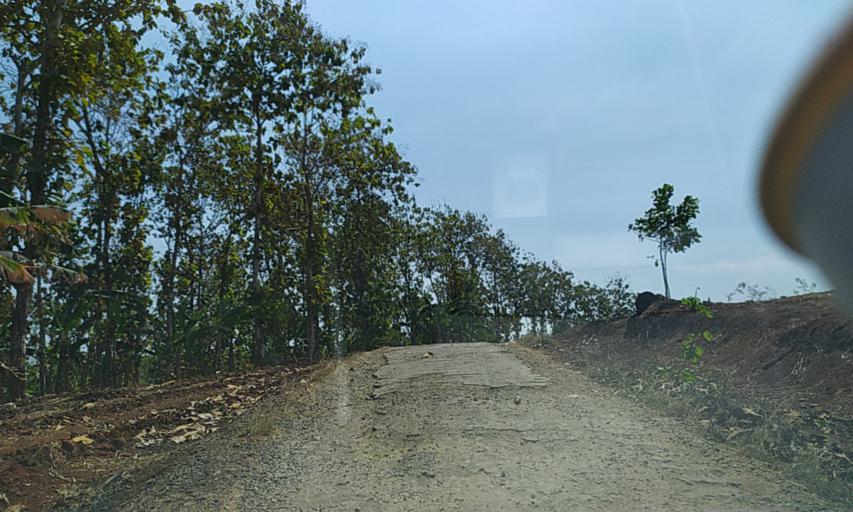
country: ID
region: Central Java
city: Prapagan
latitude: -7.5847
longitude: 108.9794
